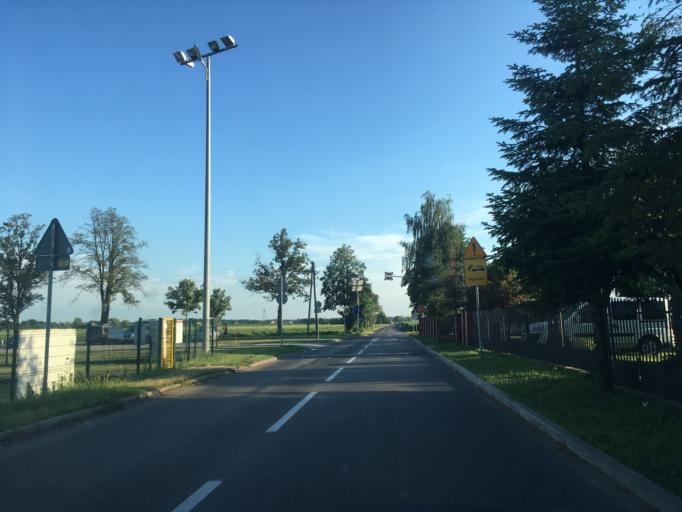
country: PL
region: Masovian Voivodeship
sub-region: Powiat grodziski
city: Grodzisk Mazowiecki
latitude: 52.1323
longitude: 20.5880
